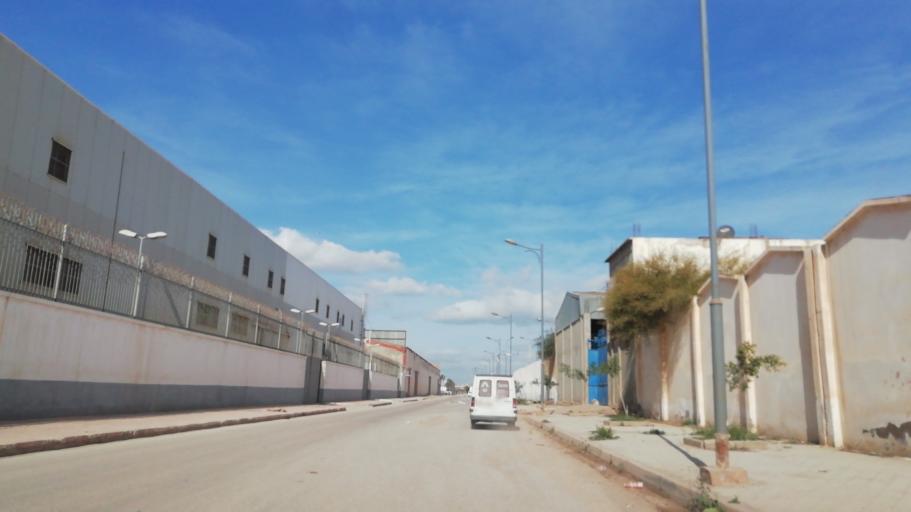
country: DZ
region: Oran
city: Es Senia
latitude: 35.6485
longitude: -0.5896
